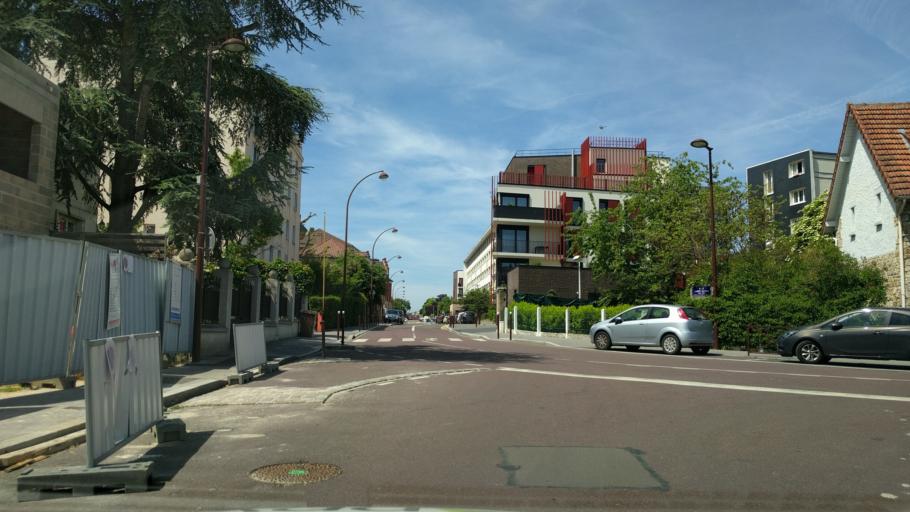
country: FR
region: Ile-de-France
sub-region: Departement des Yvelines
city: Viroflay
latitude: 48.8067
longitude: 2.1585
